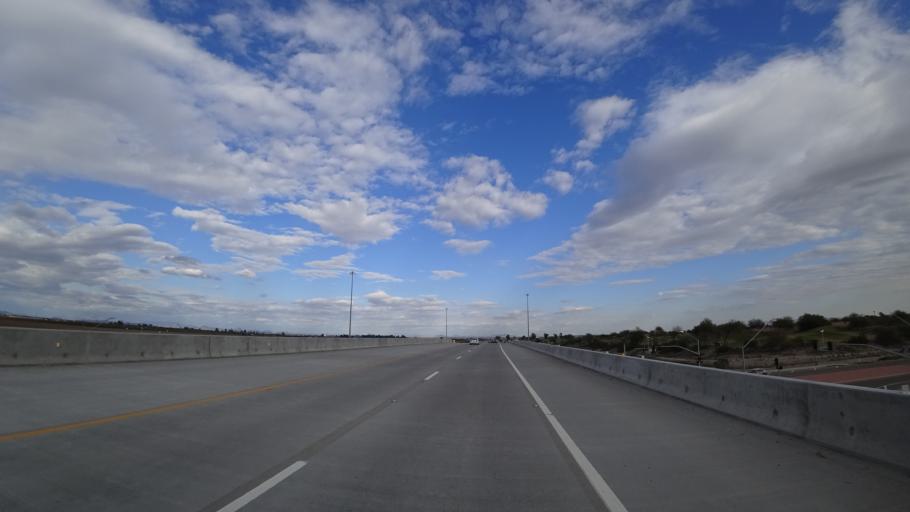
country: US
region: Arizona
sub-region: Maricopa County
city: Citrus Park
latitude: 33.5591
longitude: -112.3944
